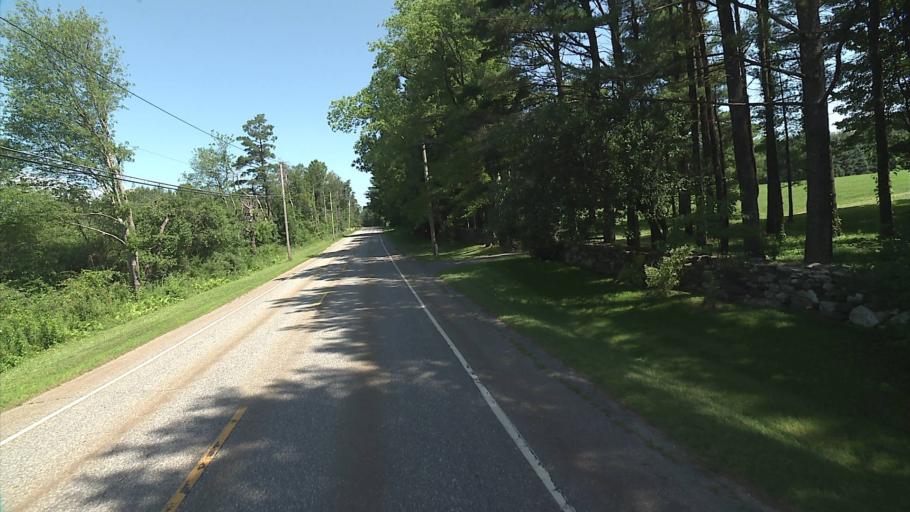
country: US
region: Connecticut
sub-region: Litchfield County
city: New Preston
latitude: 41.7622
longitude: -73.3529
